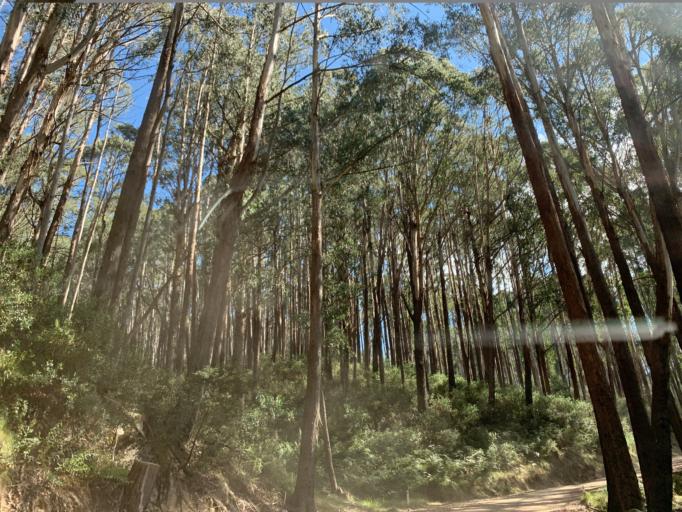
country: AU
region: Victoria
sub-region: Mansfield
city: Mansfield
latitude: -37.0983
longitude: 146.4705
